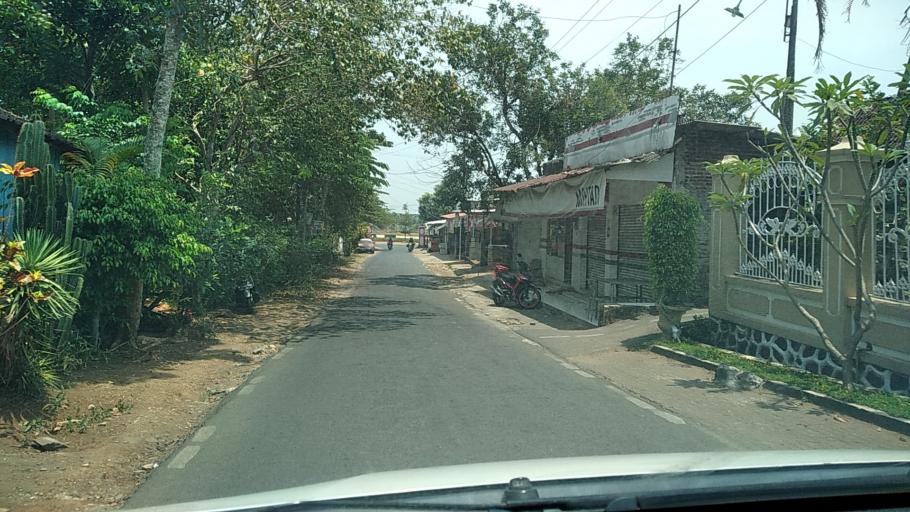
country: ID
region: Central Java
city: Ungaran
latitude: -7.0920
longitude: 110.3178
